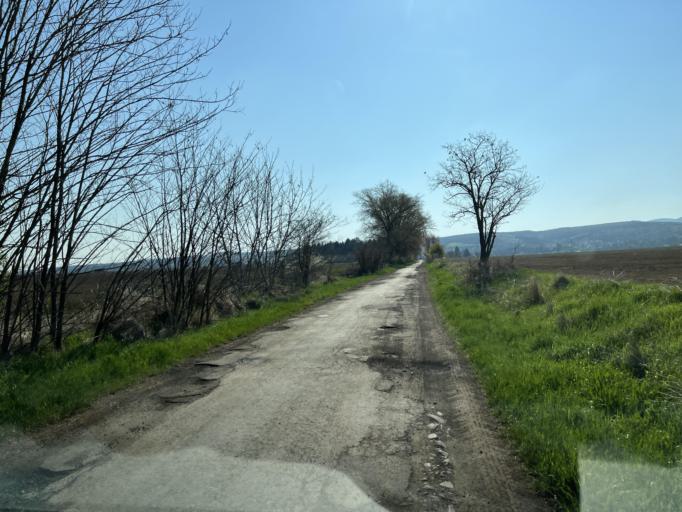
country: SK
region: Nitriansky
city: Sahy
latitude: 48.0444
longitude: 18.8970
